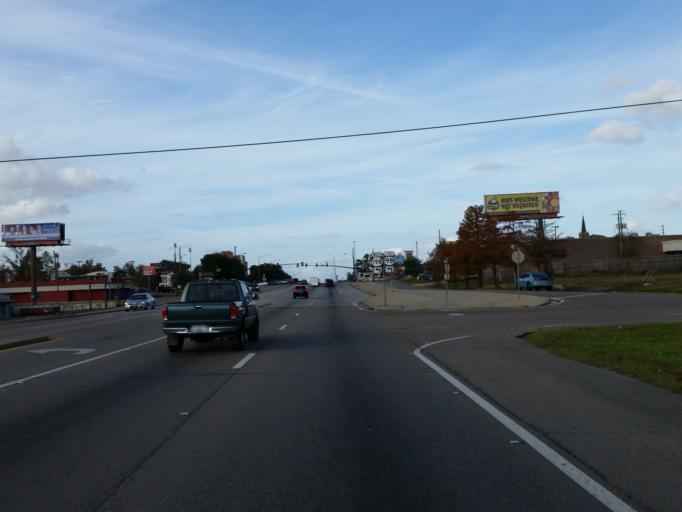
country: US
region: Mississippi
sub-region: Forrest County
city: Hattiesburg
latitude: 31.3225
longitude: -89.3289
